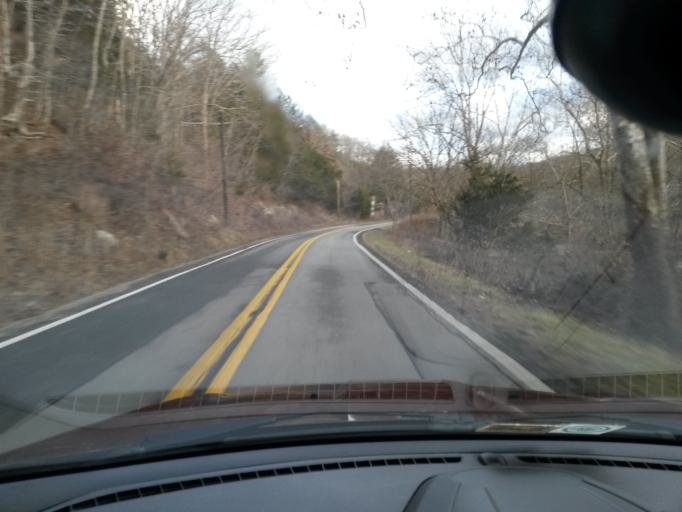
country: US
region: West Virginia
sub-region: Monroe County
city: Union
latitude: 37.5473
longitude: -80.5856
